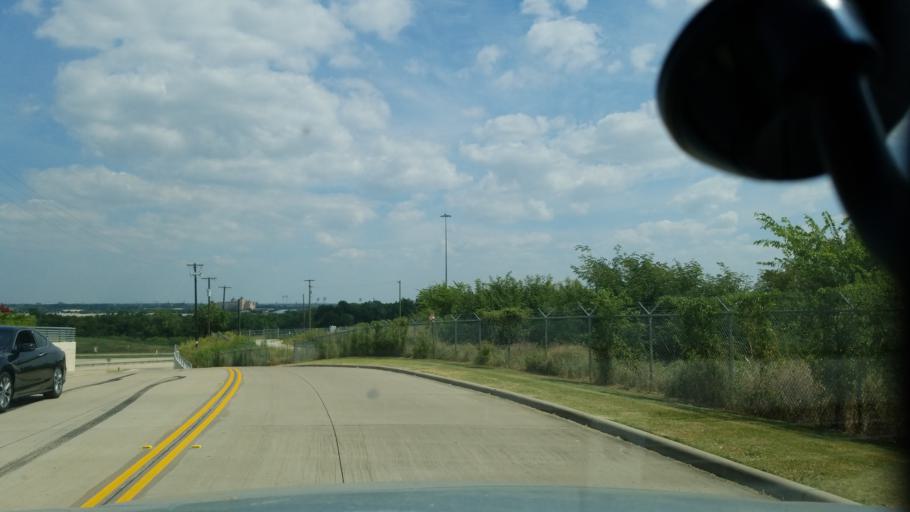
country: US
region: Texas
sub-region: Dallas County
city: Grand Prairie
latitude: 32.7567
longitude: -96.9858
